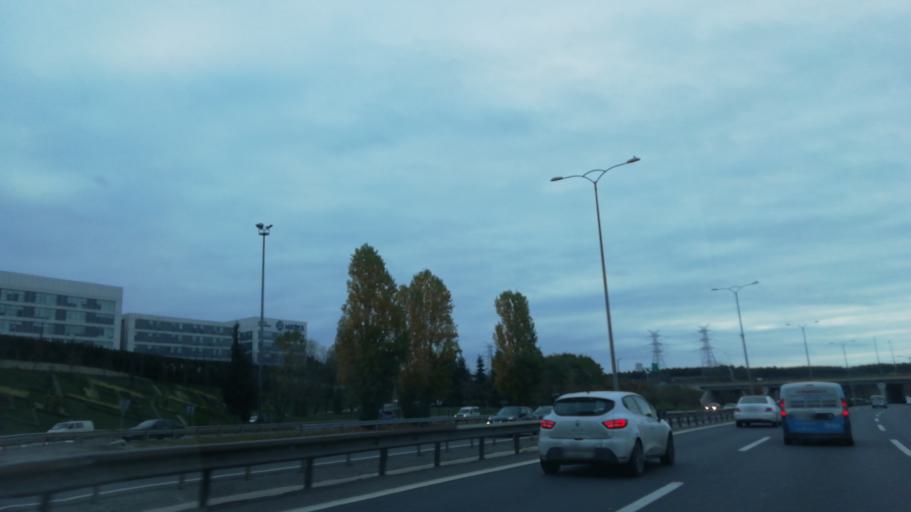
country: TR
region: Istanbul
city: Umraniye
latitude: 41.0903
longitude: 29.0895
